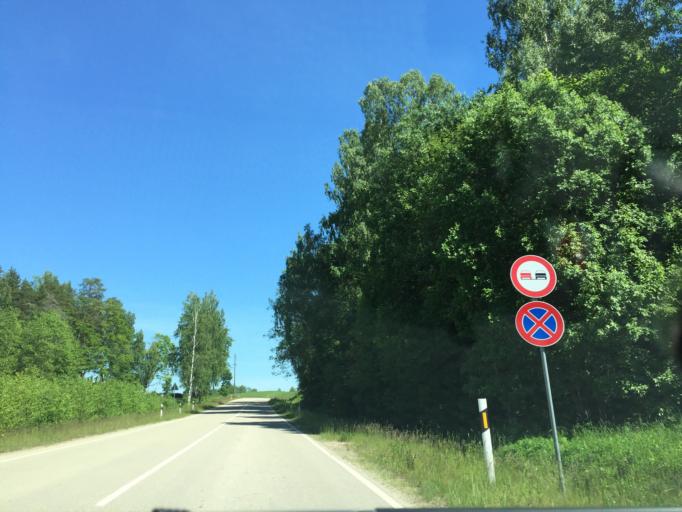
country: LV
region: Preilu Rajons
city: Jaunaglona
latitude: 56.2350
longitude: 27.2386
